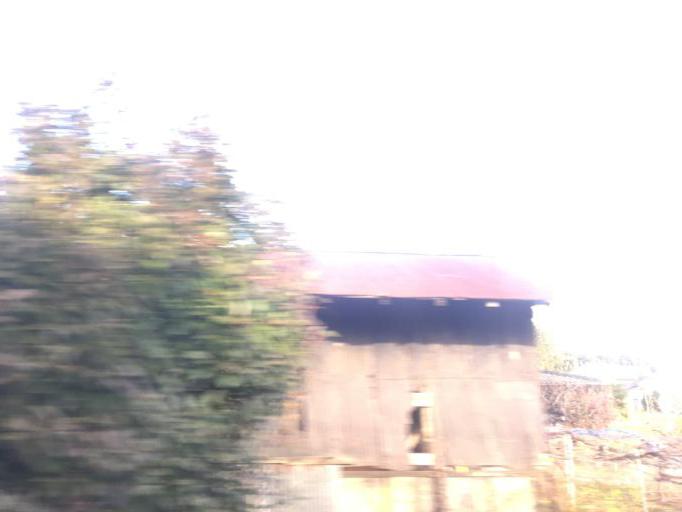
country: JP
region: Fukushima
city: Hobaramachi
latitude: 37.8084
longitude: 140.5248
